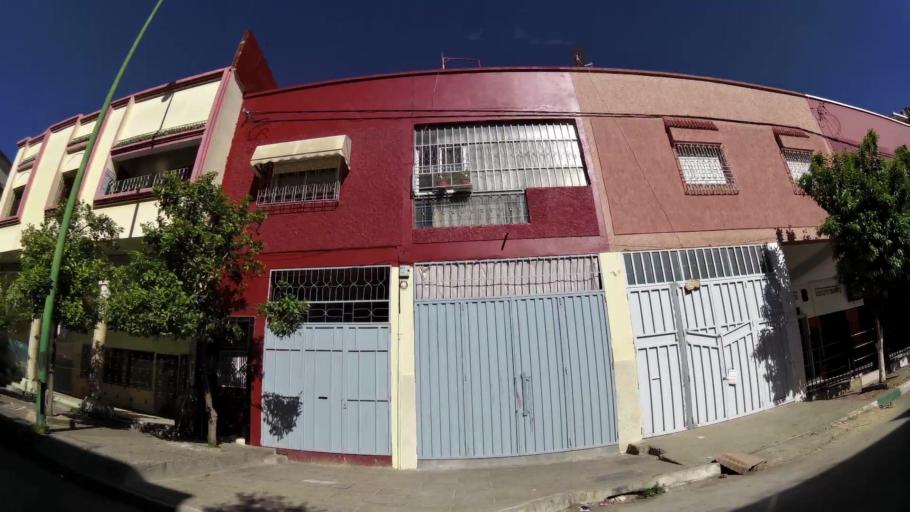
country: MA
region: Meknes-Tafilalet
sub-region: Meknes
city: Meknes
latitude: 33.8942
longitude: -5.5000
